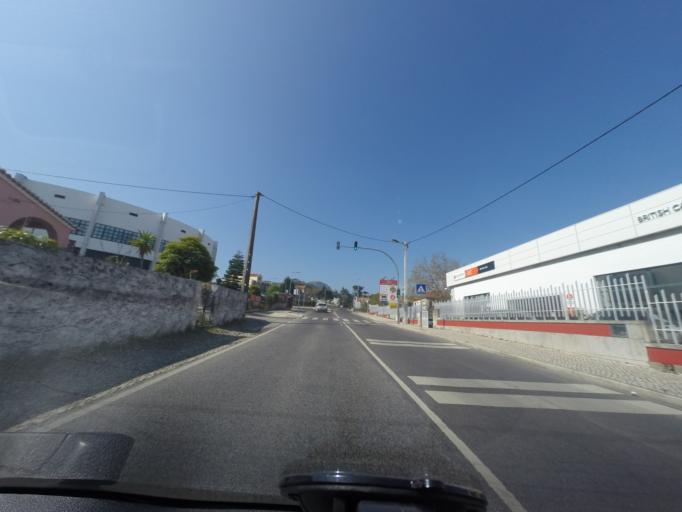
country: PT
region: Lisbon
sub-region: Sintra
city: Sintra
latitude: 38.8083
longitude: -9.3776
